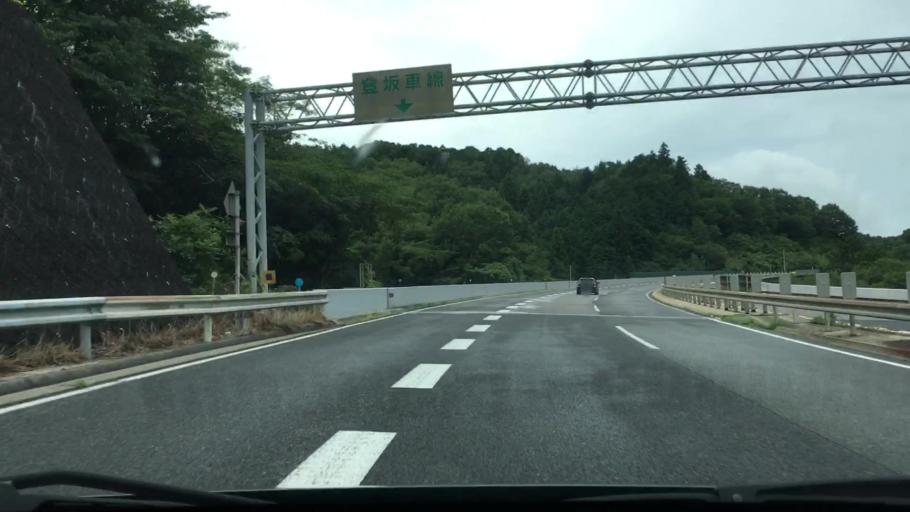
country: JP
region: Hiroshima
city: Hiroshima-shi
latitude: 34.5179
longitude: 132.4268
